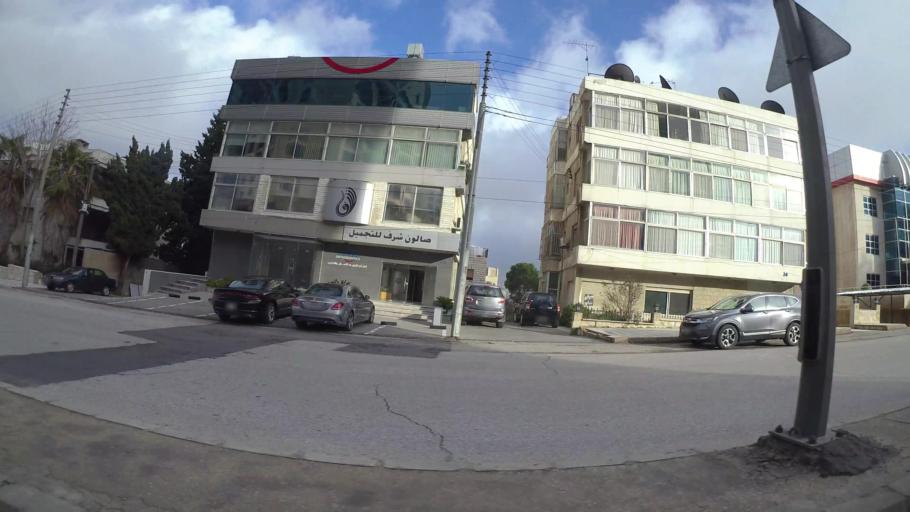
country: JO
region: Amman
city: Wadi as Sir
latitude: 31.9569
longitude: 35.8785
